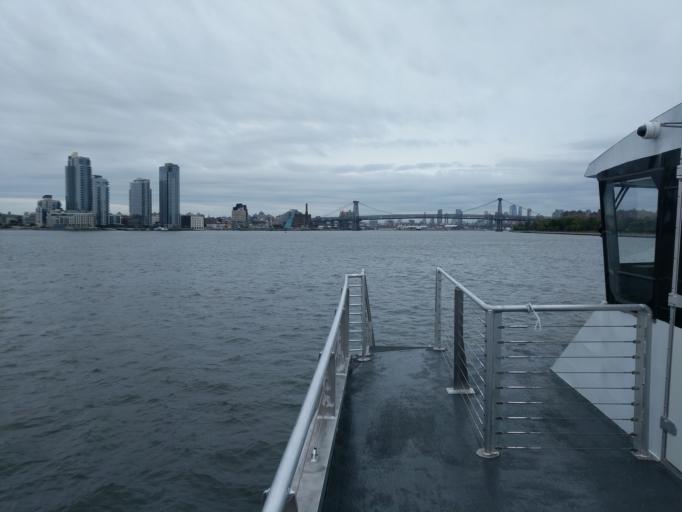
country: US
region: New York
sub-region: Queens County
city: Long Island City
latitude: 40.7290
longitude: -73.9692
